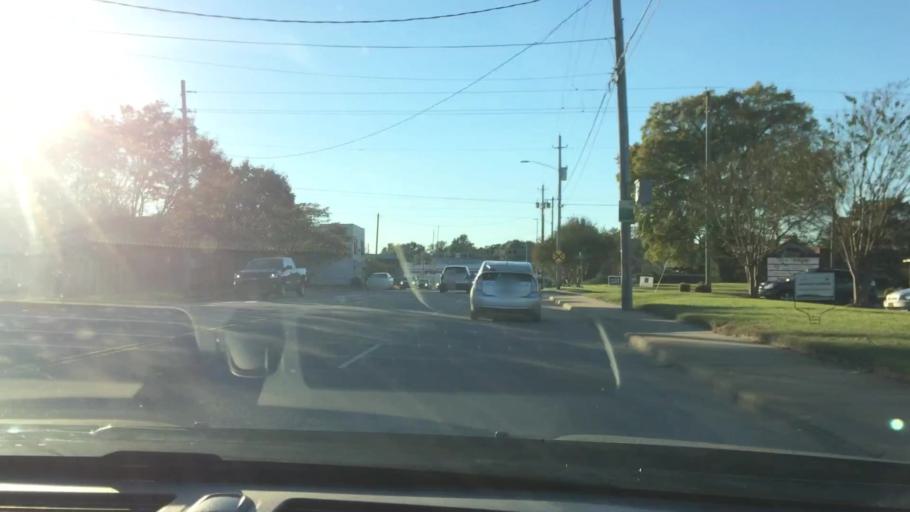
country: US
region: North Carolina
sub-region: Pitt County
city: Greenville
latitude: 35.6024
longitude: -77.3790
